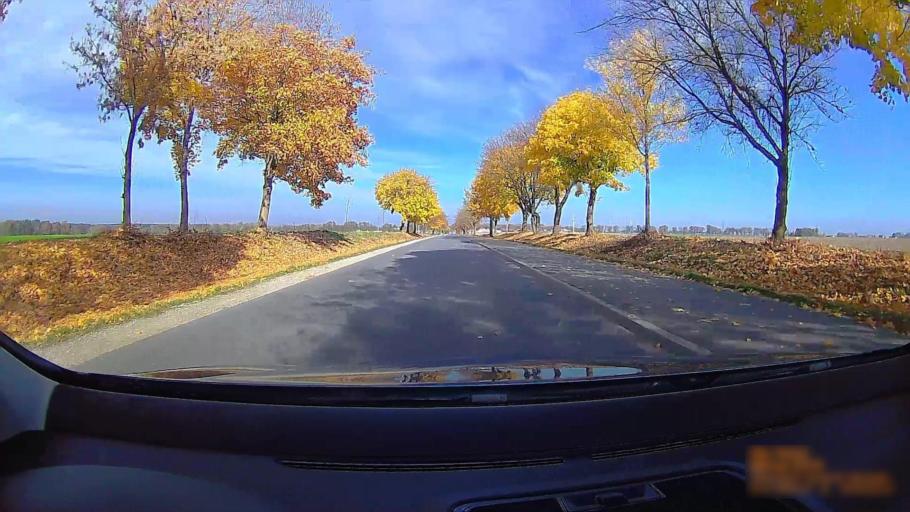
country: PL
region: Greater Poland Voivodeship
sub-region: Powiat kepinski
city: Kepno
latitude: 51.3481
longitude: 18.0256
